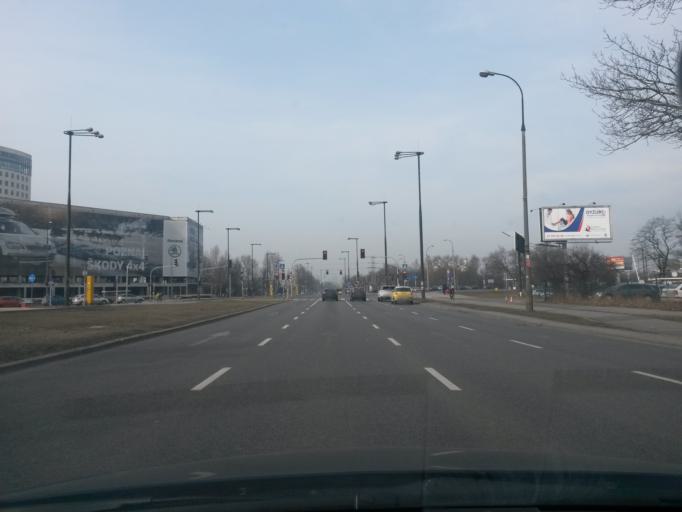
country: PL
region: Masovian Voivodeship
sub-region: Warszawa
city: Mokotow
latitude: 52.1894
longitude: 21.0480
